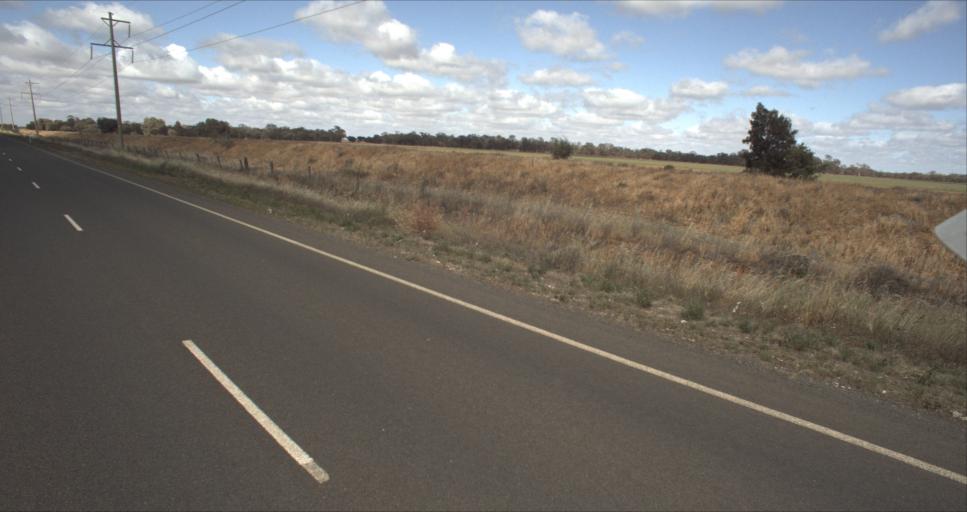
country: AU
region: New South Wales
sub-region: Murrumbidgee Shire
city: Darlington Point
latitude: -34.5370
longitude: 146.1729
